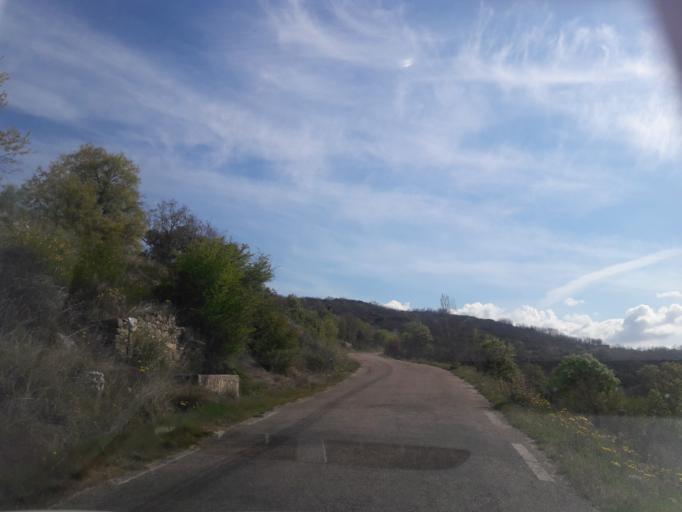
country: ES
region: Castille and Leon
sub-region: Provincia de Salamanca
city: San Esteban de la Sierra
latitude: 40.5071
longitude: -5.8816
